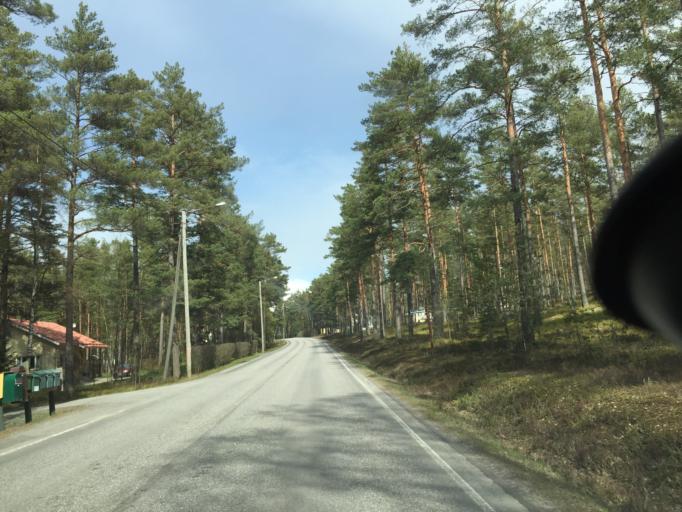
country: FI
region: Varsinais-Suomi
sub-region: Salo
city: Saerkisalo
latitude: 59.9786
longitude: 23.0108
